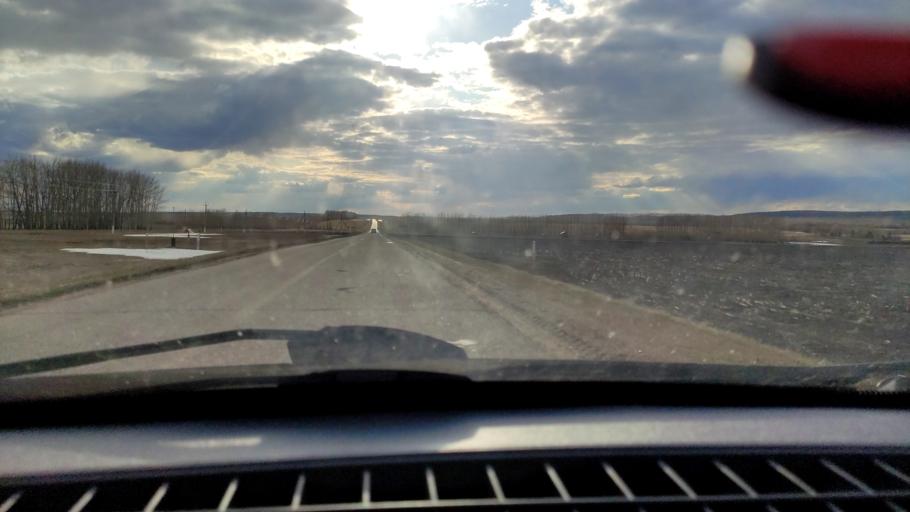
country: RU
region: Bashkortostan
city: Karmaskaly
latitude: 54.3487
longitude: 56.0580
